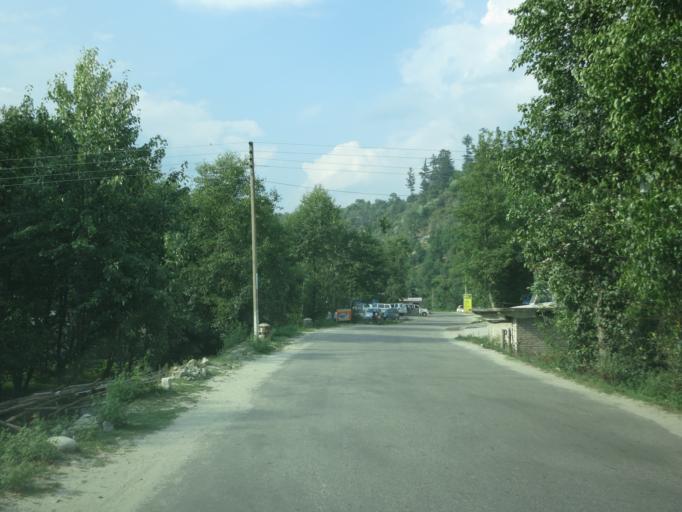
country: IN
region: Himachal Pradesh
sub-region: Kulu
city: Nagar
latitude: 32.1085
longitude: 77.1508
